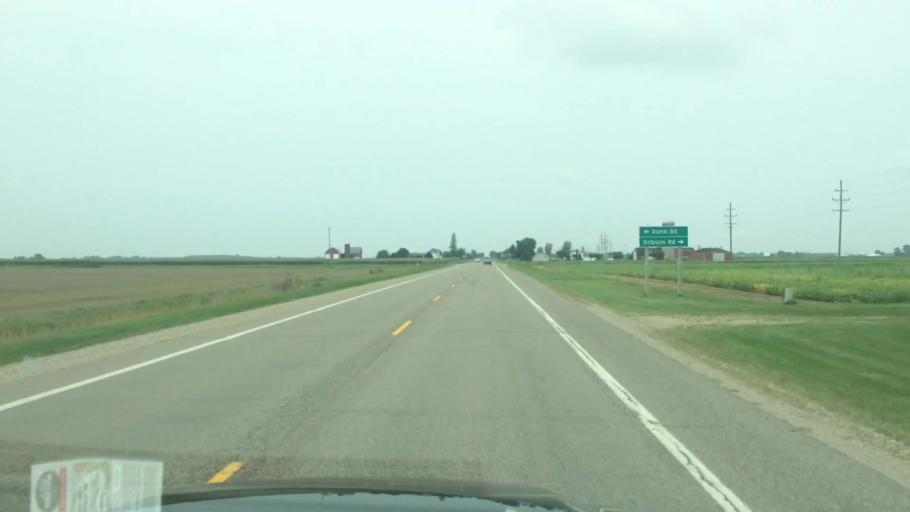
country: US
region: Michigan
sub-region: Huron County
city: Bad Axe
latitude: 43.9078
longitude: -83.0038
